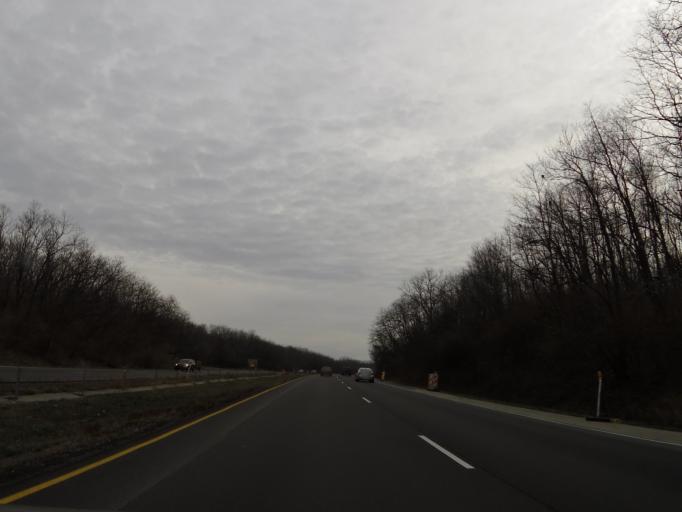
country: US
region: Illinois
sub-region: Vermilion County
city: Oakwood
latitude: 40.1274
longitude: -87.7260
